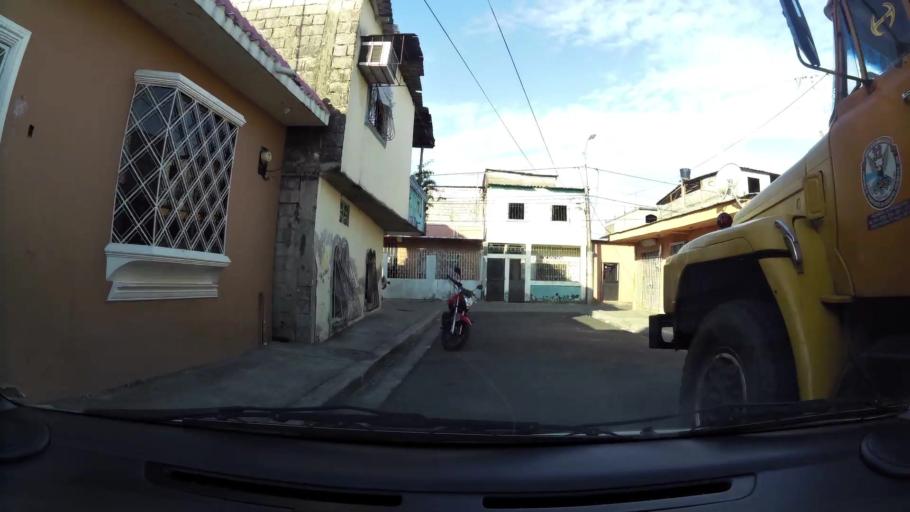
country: EC
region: Guayas
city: Guayaquil
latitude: -2.2286
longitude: -79.9081
